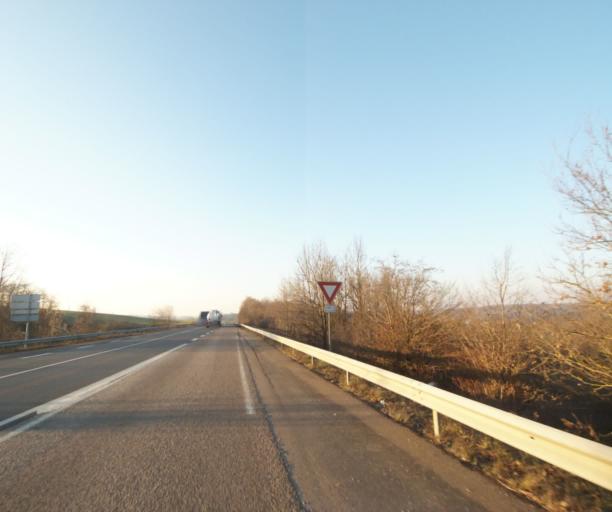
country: FR
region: Champagne-Ardenne
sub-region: Departement de la Haute-Marne
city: Chevillon
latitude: 48.5423
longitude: 5.0837
